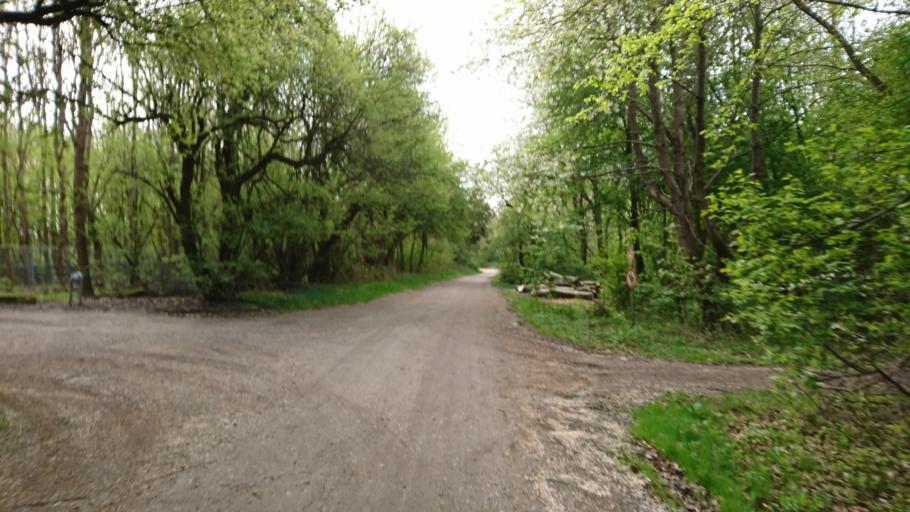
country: DK
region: Capital Region
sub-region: Ballerup Kommune
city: Ballerup
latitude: 55.7451
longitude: 12.3986
